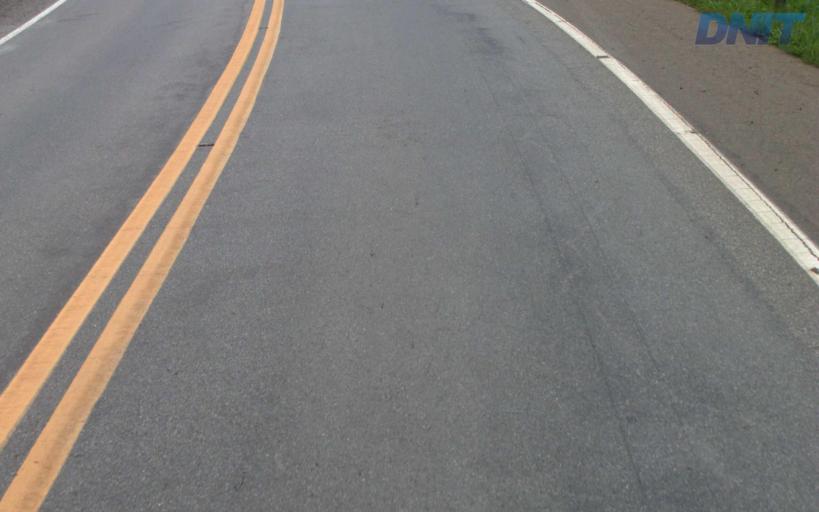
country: BR
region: Minas Gerais
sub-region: Belo Oriente
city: Belo Oriente
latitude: -19.0917
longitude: -42.1891
